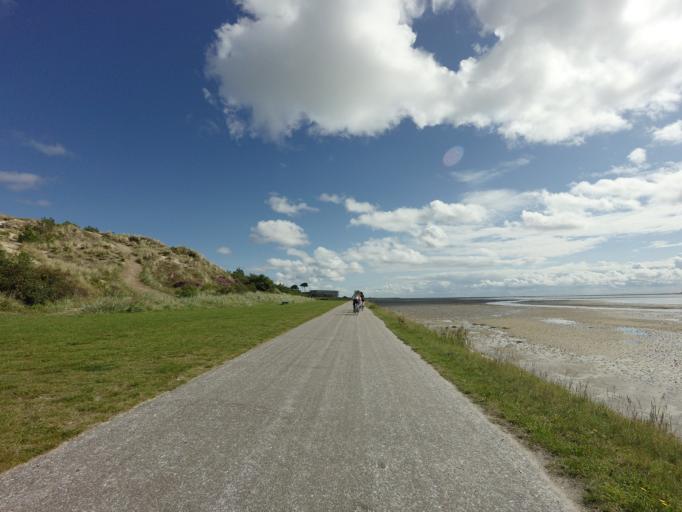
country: NL
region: Friesland
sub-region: Gemeente Terschelling
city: West-Terschelling
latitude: 53.3659
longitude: 5.2266
